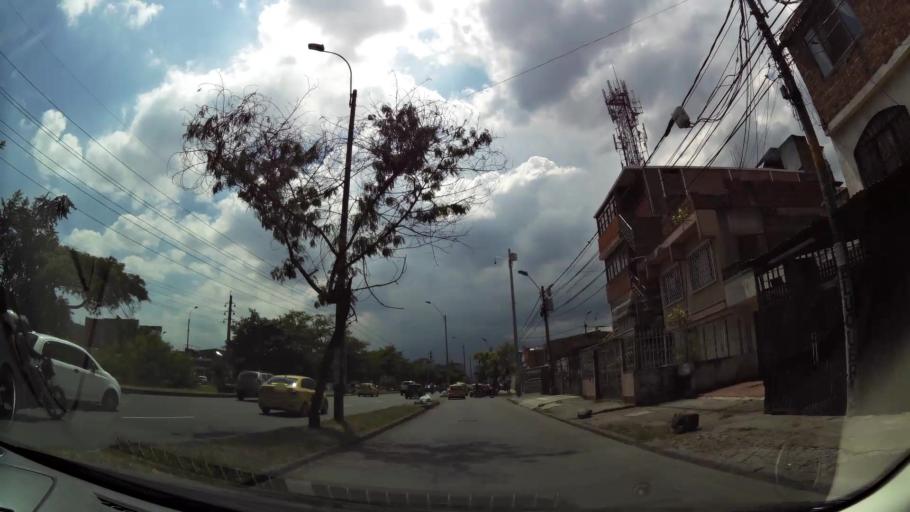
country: CO
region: Valle del Cauca
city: Cali
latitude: 3.4380
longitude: -76.5083
